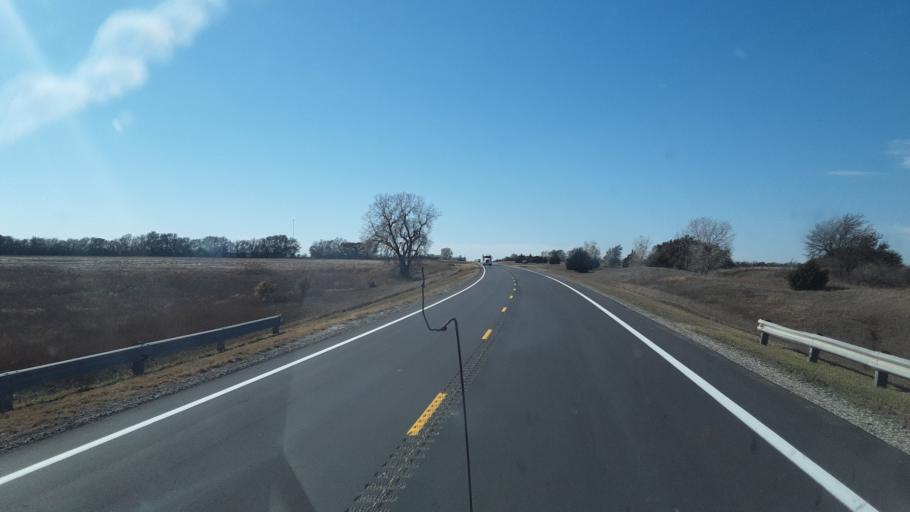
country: US
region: Kansas
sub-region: Rice County
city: Lyons
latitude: 38.3762
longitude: -98.1246
